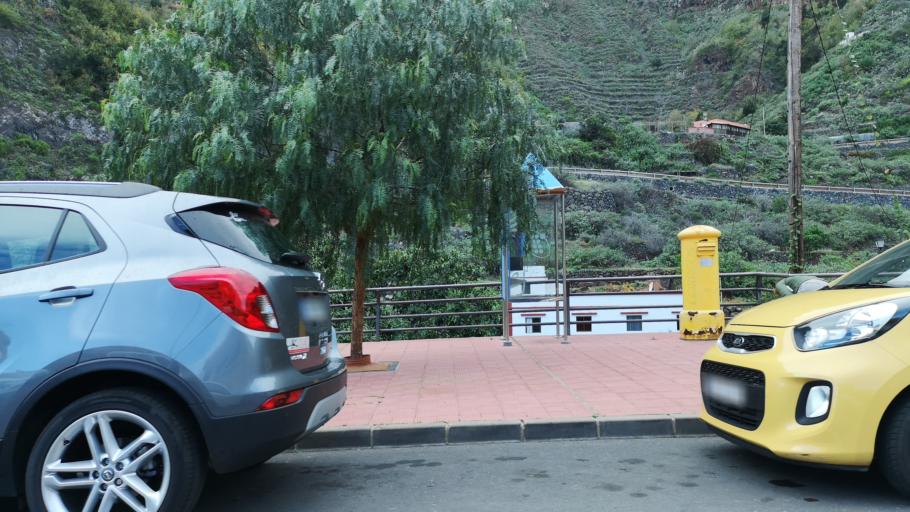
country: ES
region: Canary Islands
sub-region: Provincia de Santa Cruz de Tenerife
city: Agulo
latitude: 28.1861
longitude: -17.1948
